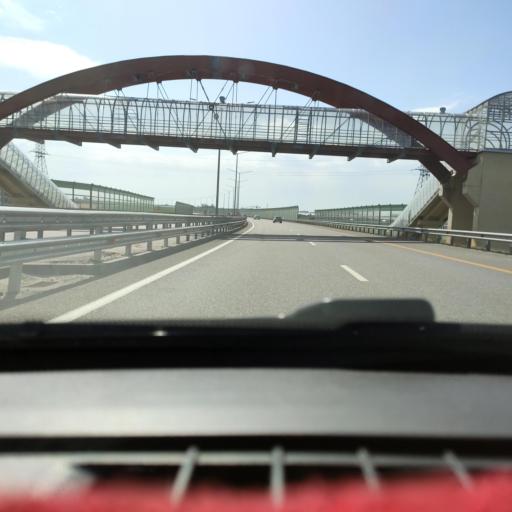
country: RU
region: Voronezj
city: Novaya Usman'
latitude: 51.6068
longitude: 39.3246
